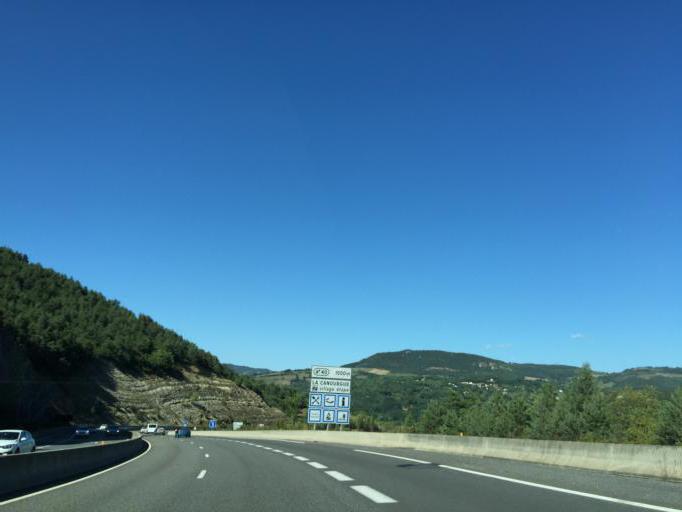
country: FR
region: Languedoc-Roussillon
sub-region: Departement de la Lozere
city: La Canourgue
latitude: 44.4253
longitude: 3.1863
